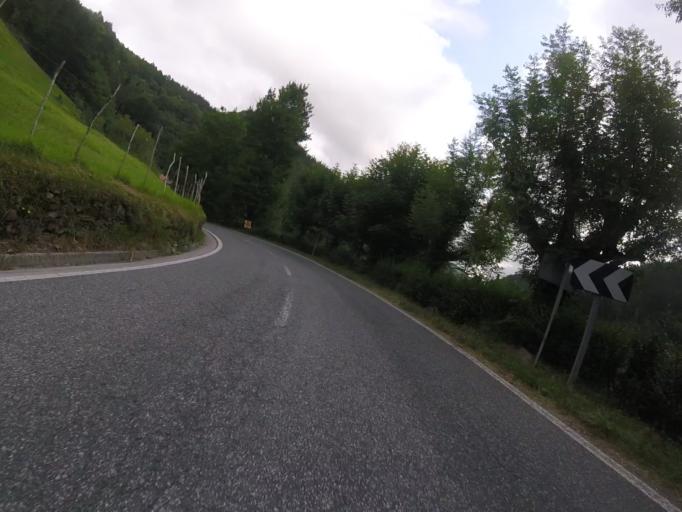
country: ES
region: Navarre
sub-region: Provincia de Navarra
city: Eratsun
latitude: 43.0888
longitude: -1.7920
